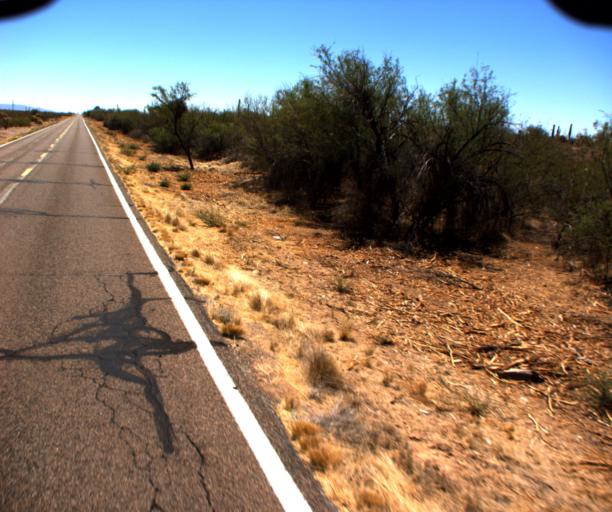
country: US
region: Arizona
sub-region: Pima County
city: Ajo
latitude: 32.2089
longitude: -112.6095
